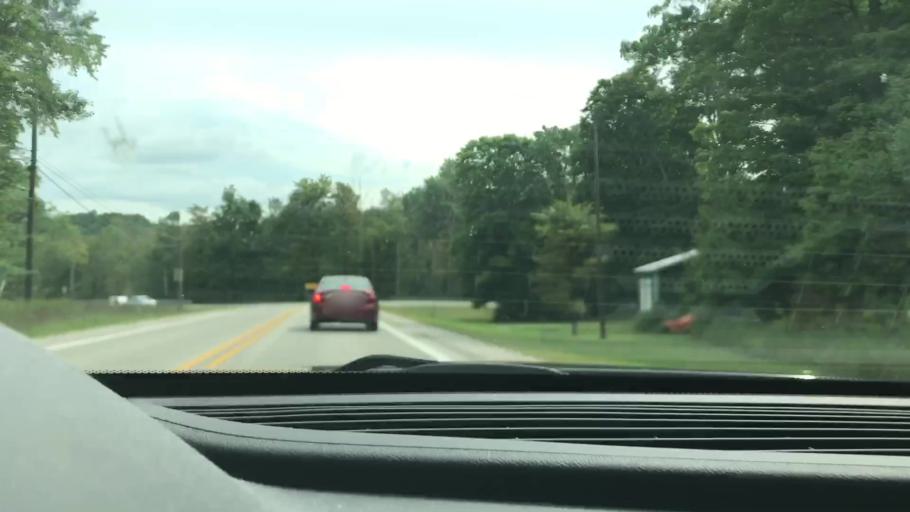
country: US
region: Michigan
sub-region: Antrim County
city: Bellaire
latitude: 45.0801
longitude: -85.2833
